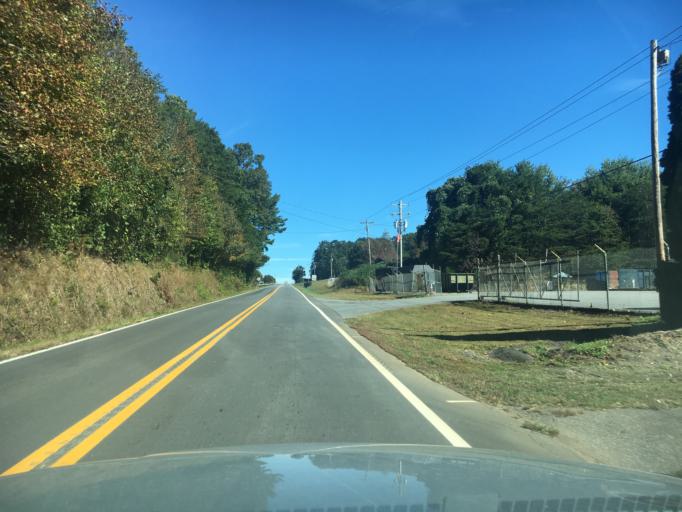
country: US
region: North Carolina
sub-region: Burke County
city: Salem
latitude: 35.6773
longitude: -81.7339
